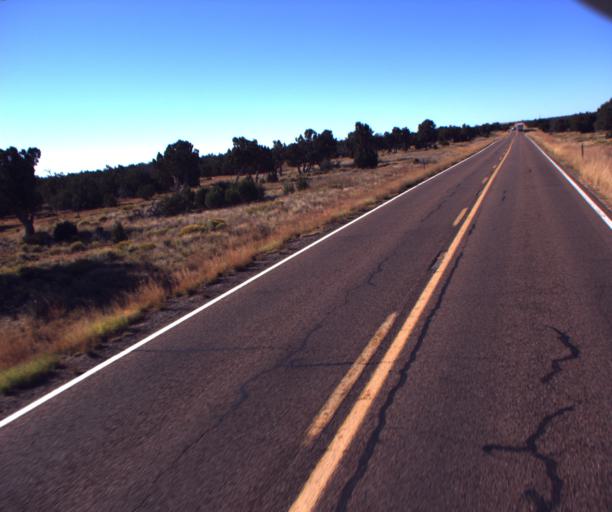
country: US
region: Arizona
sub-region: Navajo County
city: Heber-Overgaard
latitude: 34.4891
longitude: -110.4589
